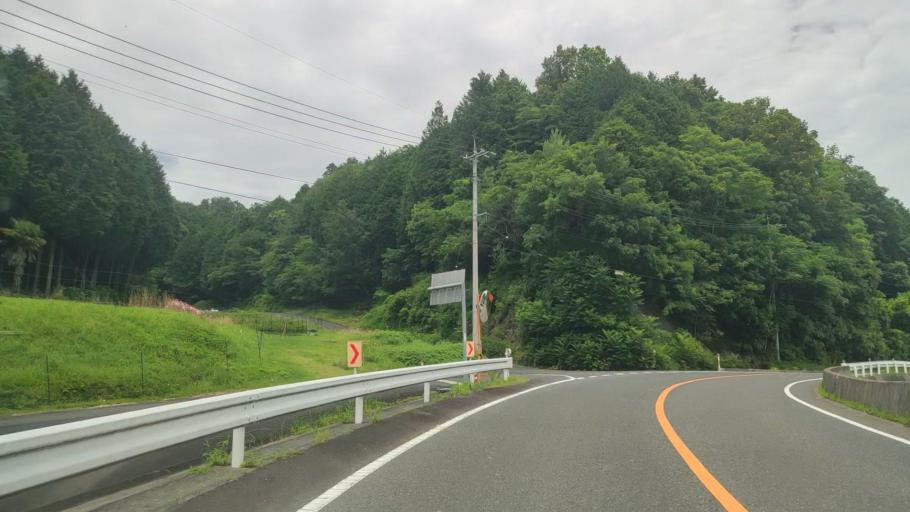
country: JP
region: Okayama
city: Tsuyama
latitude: 35.0839
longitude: 134.2502
